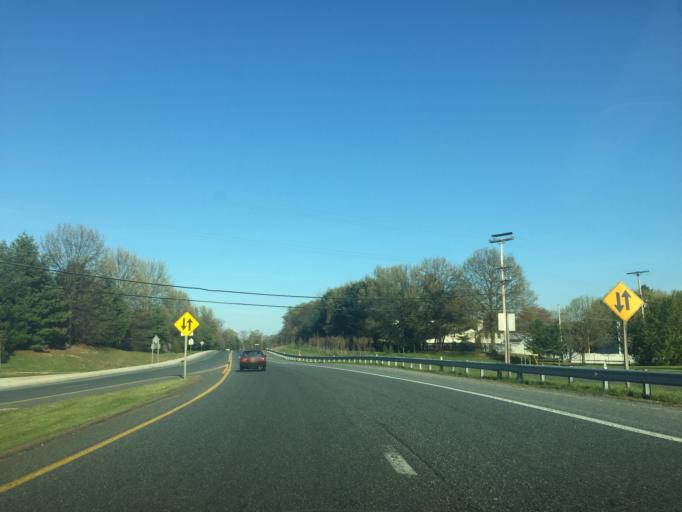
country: US
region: Maryland
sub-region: Harford County
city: Riverside
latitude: 39.4775
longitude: -76.2466
